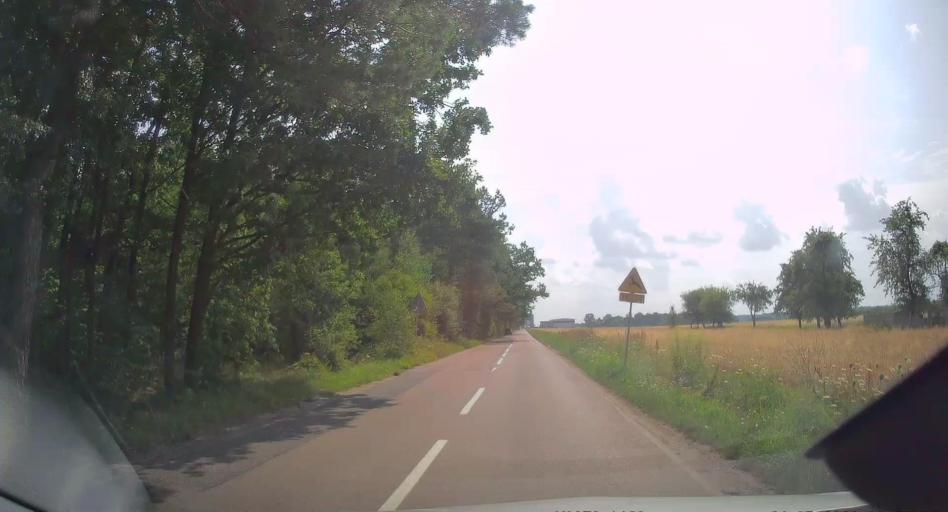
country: PL
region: Lodz Voivodeship
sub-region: Powiat tomaszowski
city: Lubochnia
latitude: 51.5759
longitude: 20.0733
